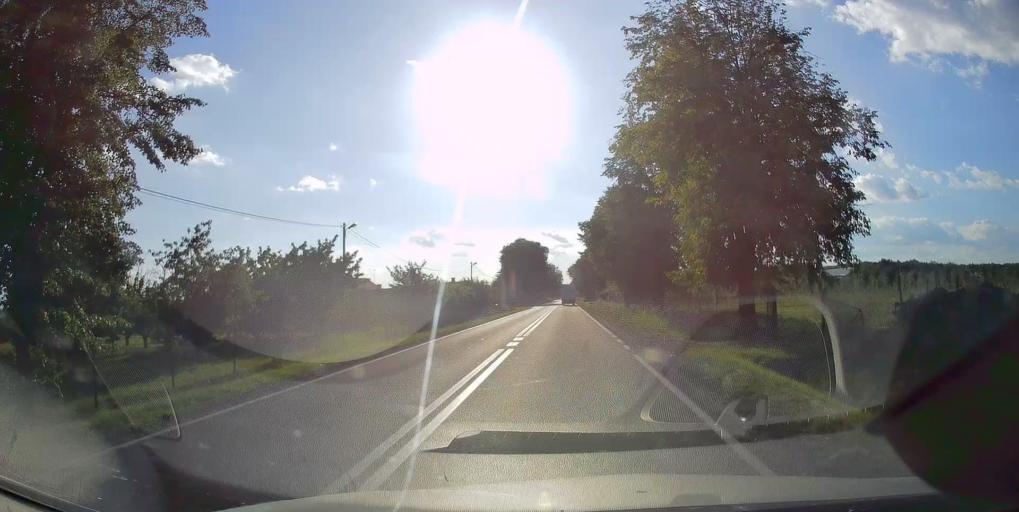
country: PL
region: Masovian Voivodeship
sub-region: Powiat grojecki
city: Bledow
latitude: 51.8025
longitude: 20.6053
